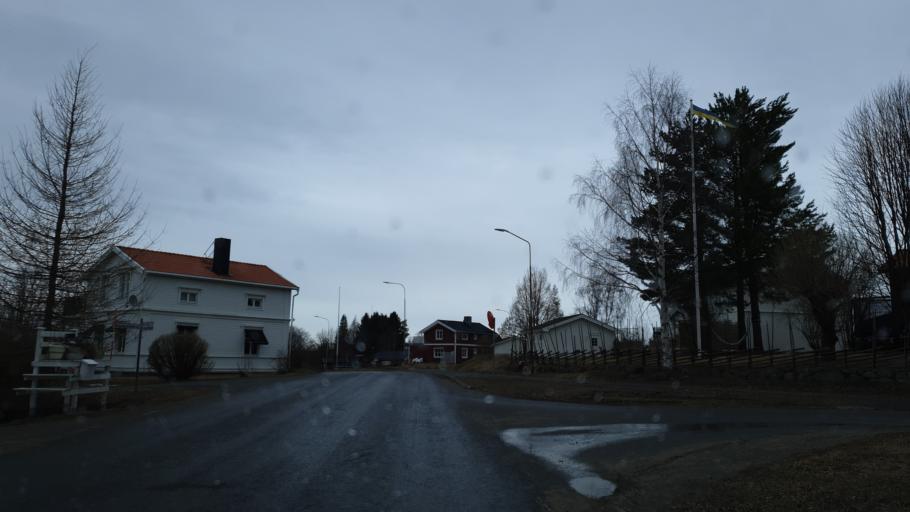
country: SE
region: Vaesterbotten
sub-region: Skelleftea Kommun
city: Kage
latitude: 64.8307
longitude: 20.9883
